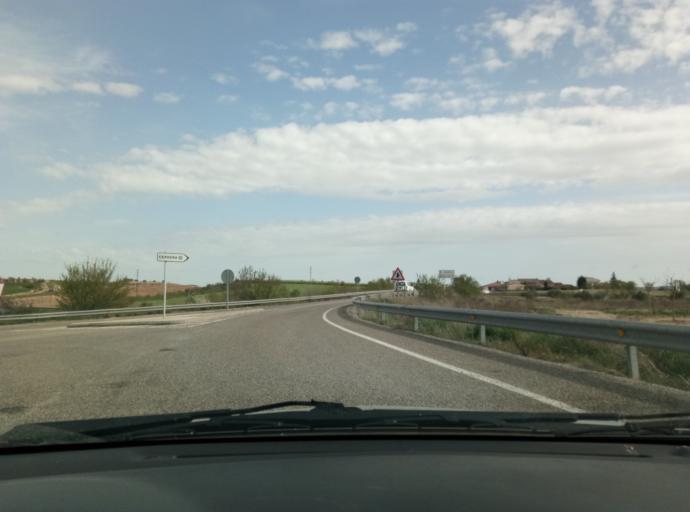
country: ES
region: Catalonia
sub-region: Provincia de Lleida
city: Cervera
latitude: 41.6782
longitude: 1.2845
